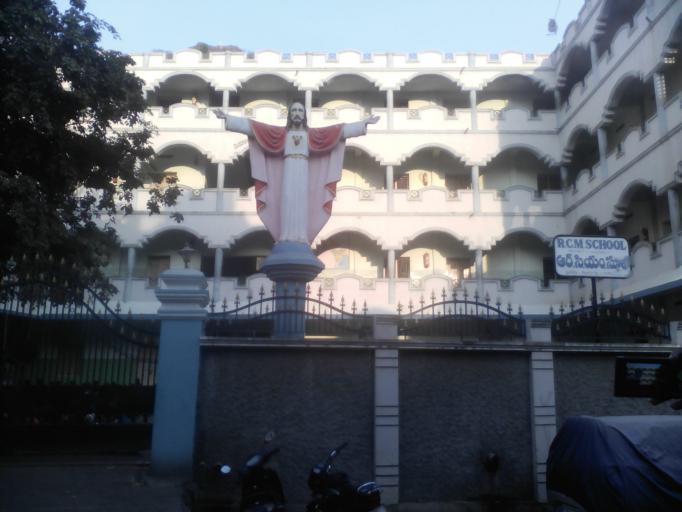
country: IN
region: Andhra Pradesh
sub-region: Krishna
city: Vijayawada
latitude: 16.5276
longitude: 80.6124
